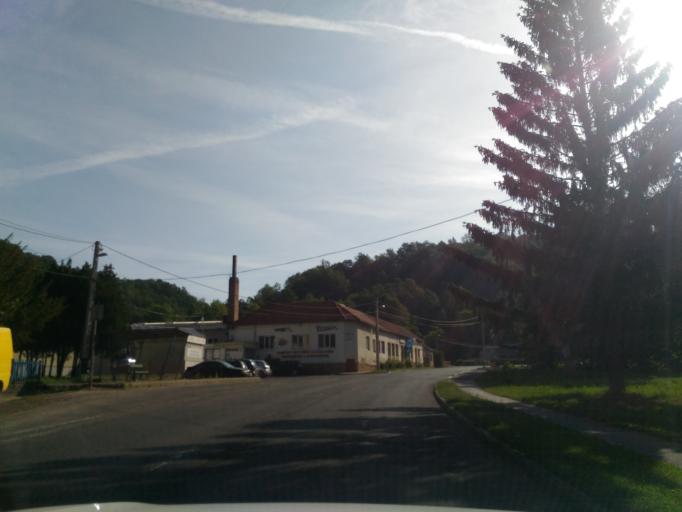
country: HU
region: Baranya
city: Komlo
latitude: 46.1913
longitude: 18.2737
